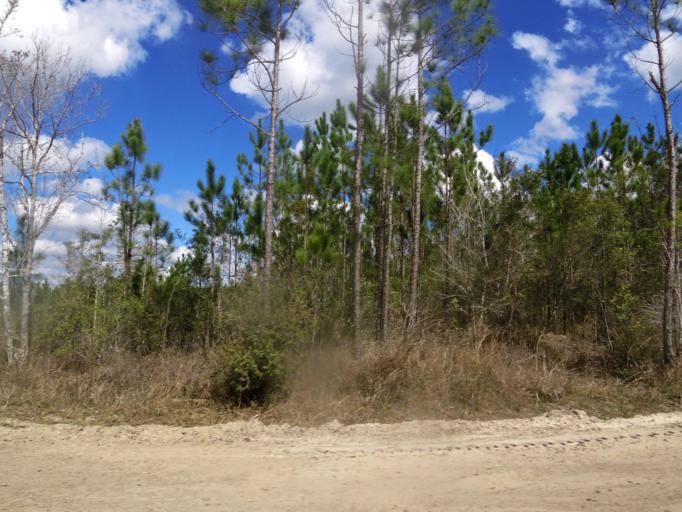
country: US
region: Florida
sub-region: Clay County
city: Green Cove Springs
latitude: 29.8368
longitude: -81.7792
